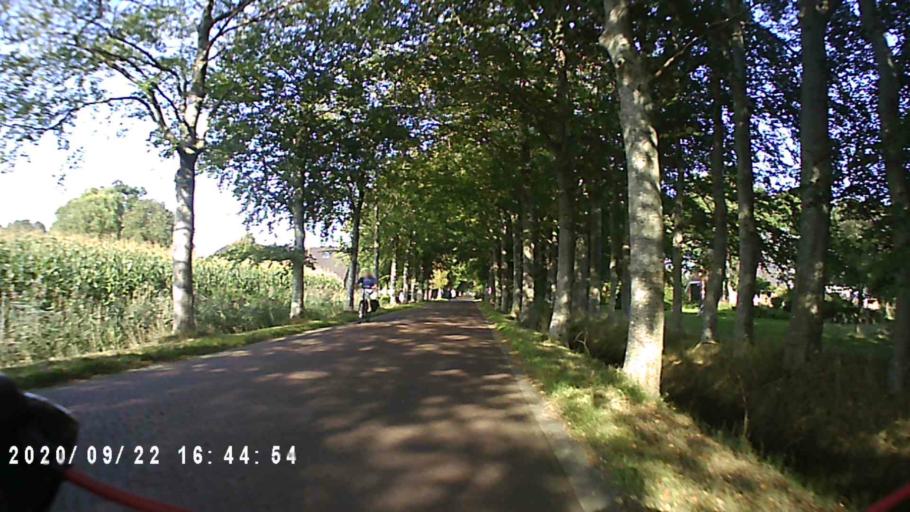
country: NL
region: Groningen
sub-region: Gemeente Leek
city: Leek
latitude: 53.1244
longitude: 6.4654
